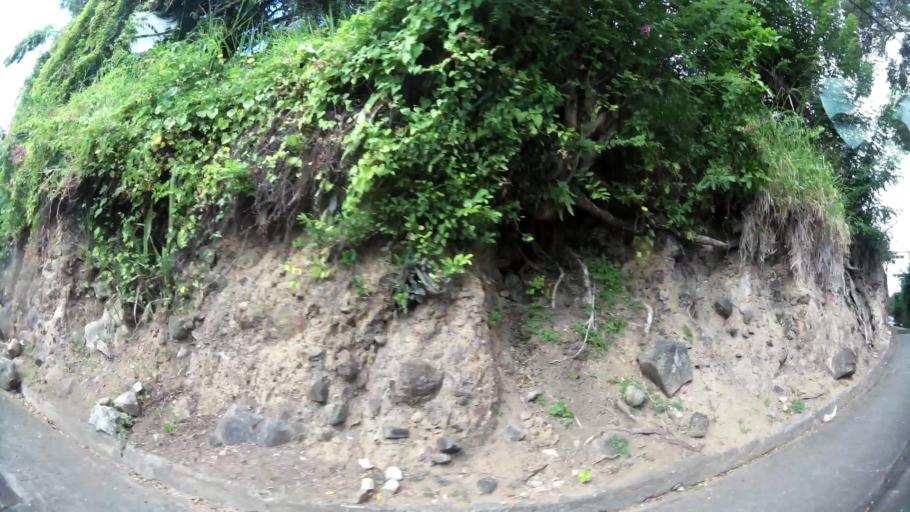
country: MQ
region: Martinique
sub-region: Martinique
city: Fort-de-France
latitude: 14.6109
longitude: -61.0681
